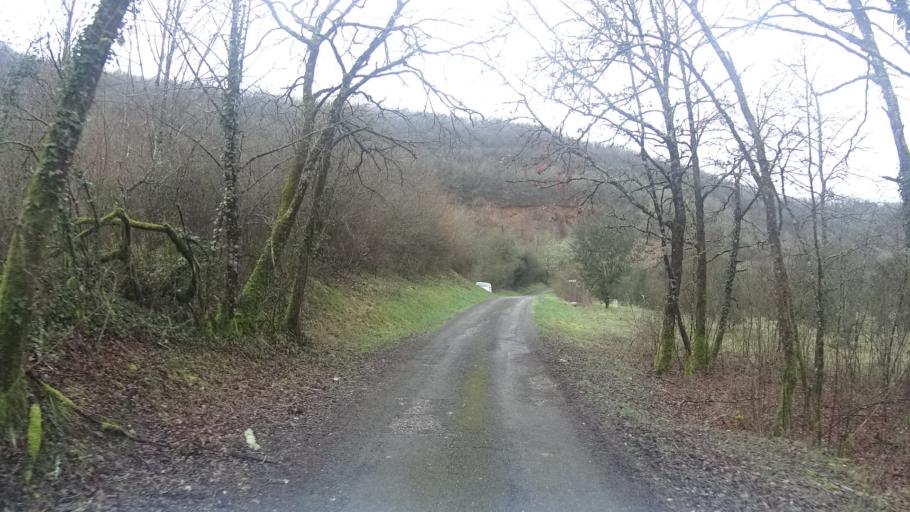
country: FR
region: Aquitaine
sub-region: Departement de la Dordogne
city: Terrasson-Lavilledieu
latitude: 45.1073
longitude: 1.2448
